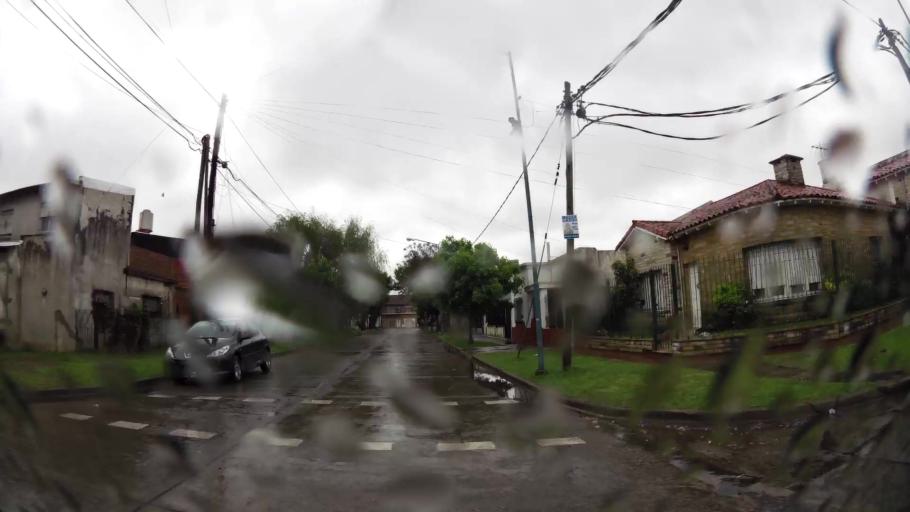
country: AR
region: Buenos Aires
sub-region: Partido de Lanus
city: Lanus
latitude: -34.7204
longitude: -58.3978
